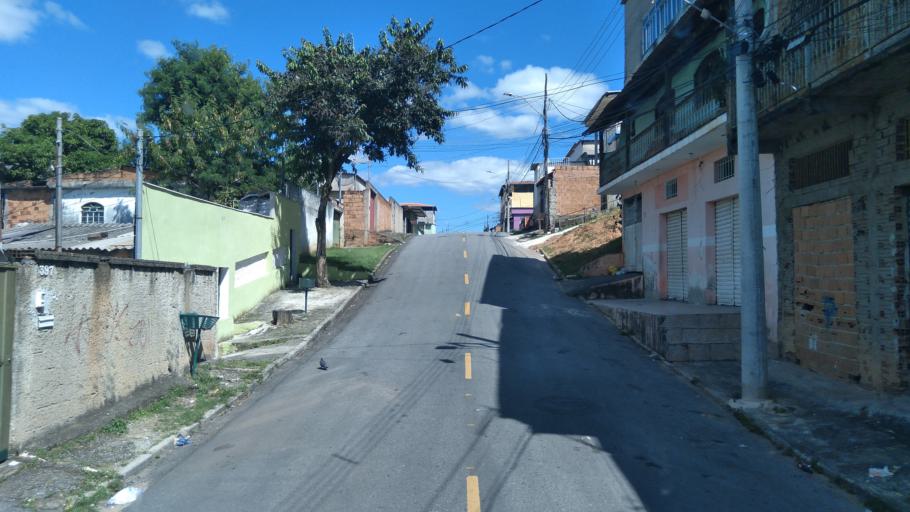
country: BR
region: Minas Gerais
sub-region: Belo Horizonte
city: Belo Horizonte
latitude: -19.8581
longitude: -43.8814
